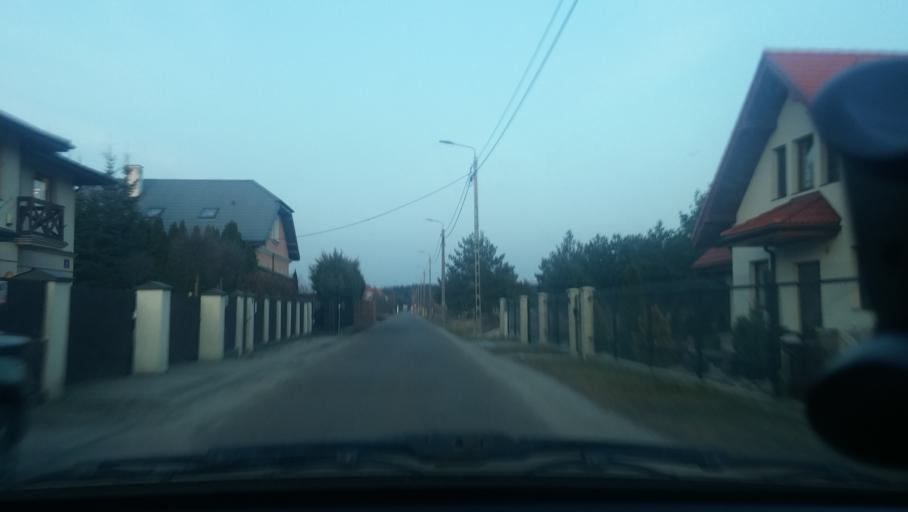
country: PL
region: Masovian Voivodeship
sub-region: Warszawa
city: Wawer
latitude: 52.1480
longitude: 21.1814
